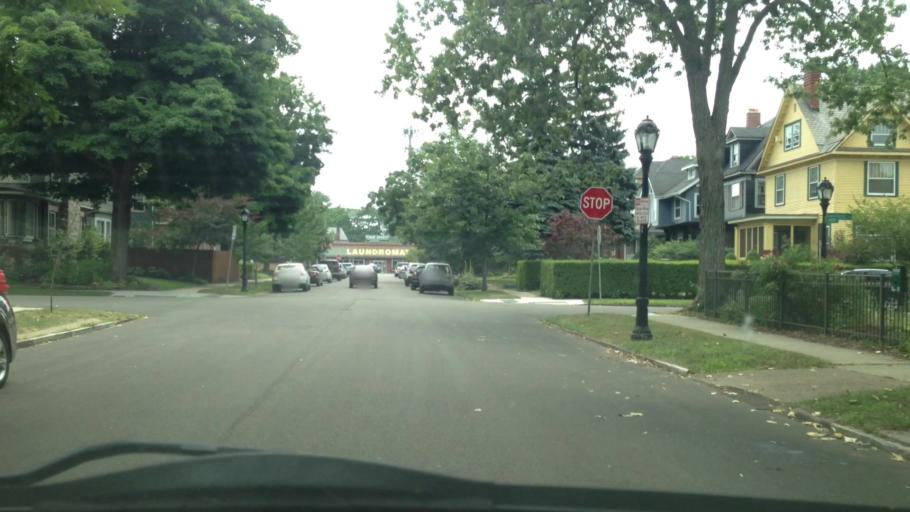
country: US
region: New York
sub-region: Erie County
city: Kenmore
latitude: 42.9332
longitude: -78.8482
